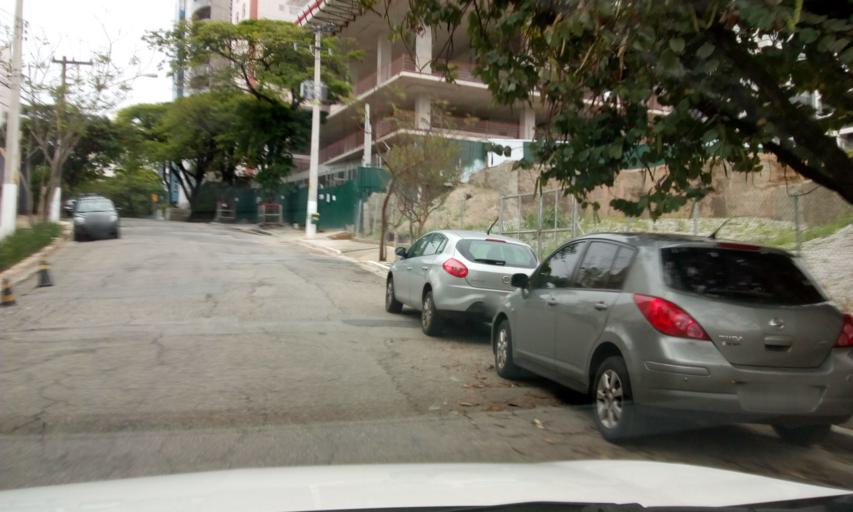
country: BR
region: Sao Paulo
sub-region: Sao Paulo
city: Sao Paulo
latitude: -23.5478
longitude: -46.6925
